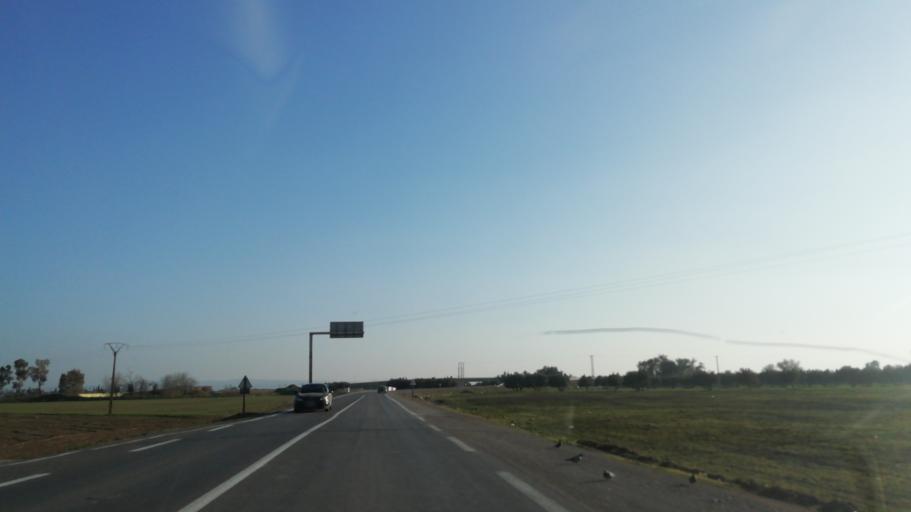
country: DZ
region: Sidi Bel Abbes
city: Sidi Bel Abbes
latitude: 35.1765
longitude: -0.6859
